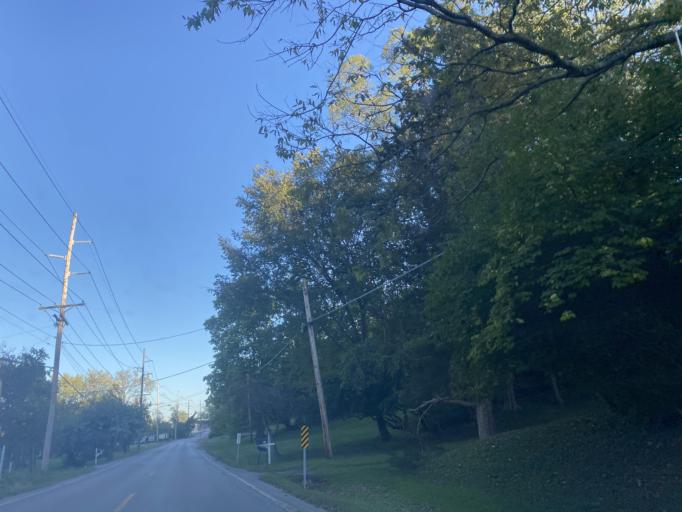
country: US
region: Kentucky
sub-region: Campbell County
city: Dayton
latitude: 39.1129
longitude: -84.4562
